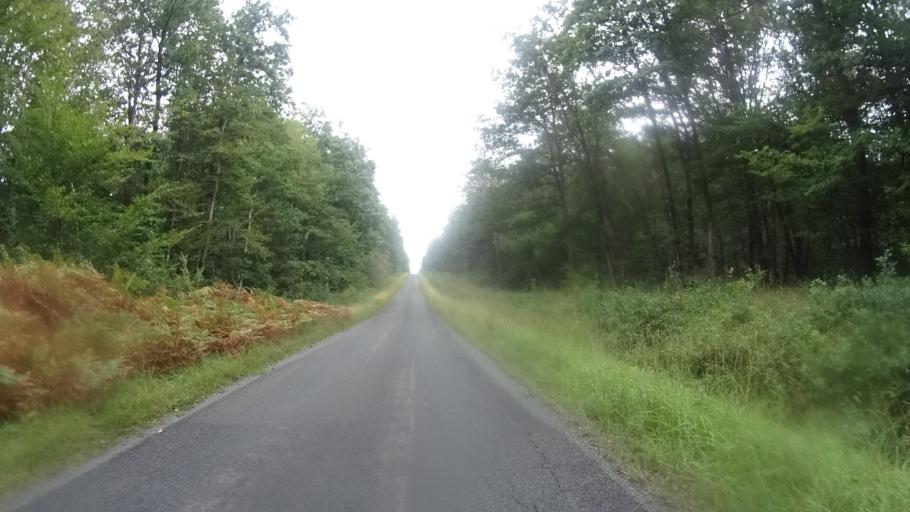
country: FR
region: Centre
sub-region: Departement du Loiret
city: Dadonville
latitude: 48.0487
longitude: 2.2700
